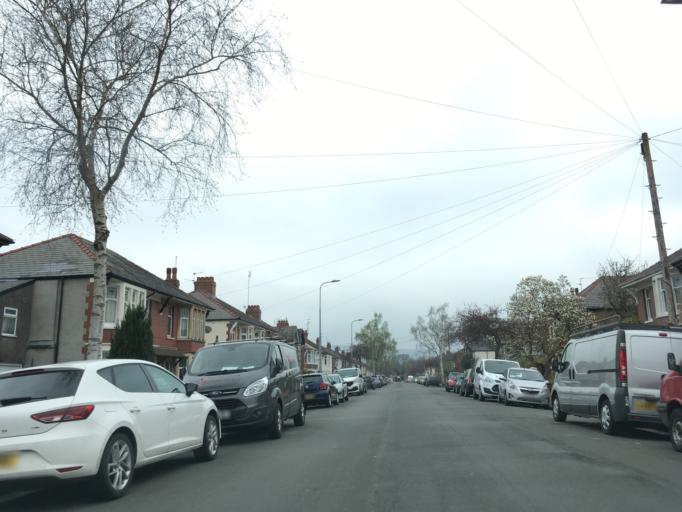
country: GB
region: Wales
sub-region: Cardiff
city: Cardiff
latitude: 51.5162
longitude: -3.1939
